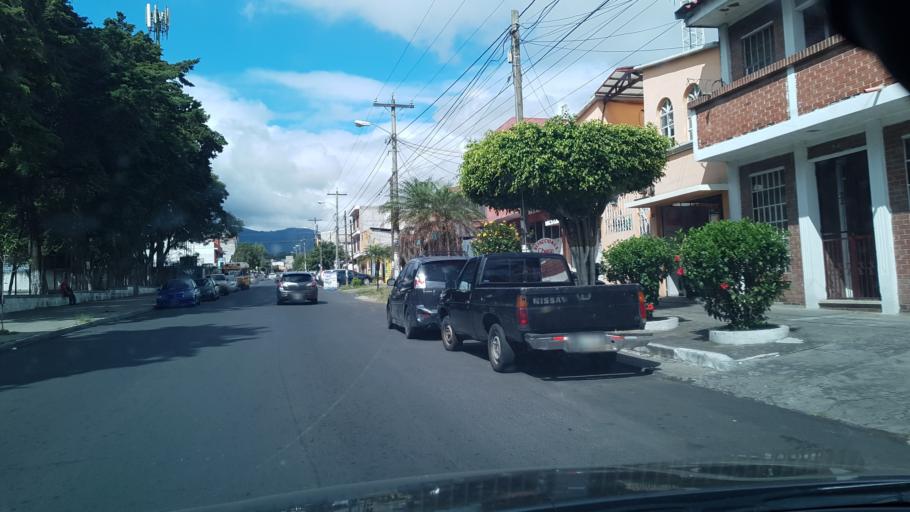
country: GT
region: Guatemala
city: Mixco
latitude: 14.6412
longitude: -90.5760
